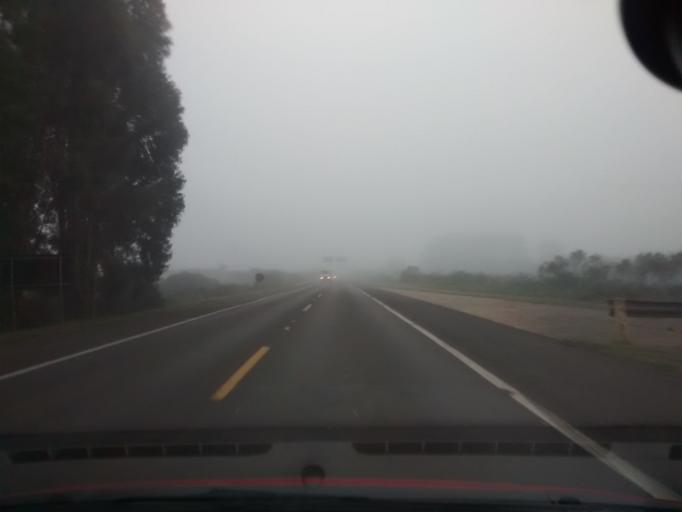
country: BR
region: Rio Grande do Sul
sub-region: Vacaria
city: Vacaria
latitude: -28.3945
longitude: -50.8496
